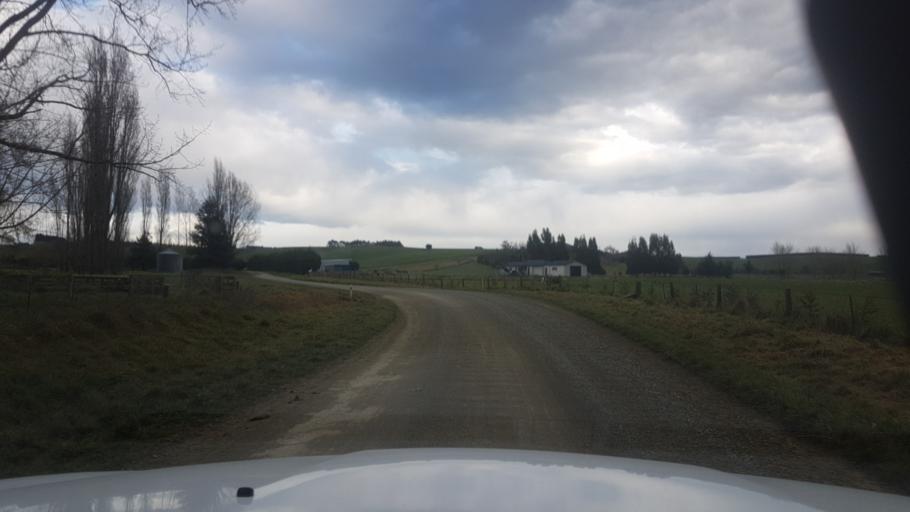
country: NZ
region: Canterbury
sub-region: Timaru District
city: Timaru
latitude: -44.3386
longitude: 171.1873
